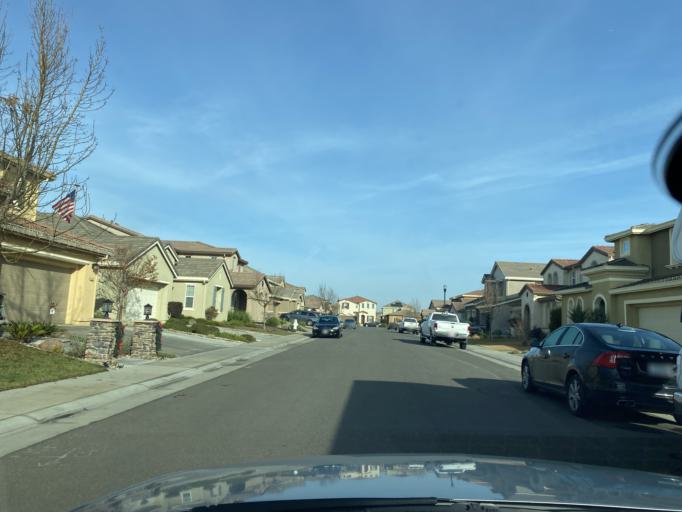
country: US
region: California
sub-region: Sacramento County
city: Elk Grove
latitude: 38.3964
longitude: -121.3932
